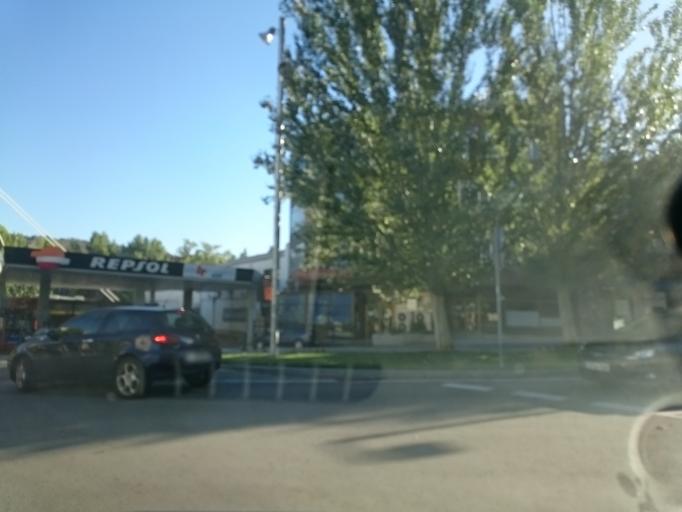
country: ES
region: Catalonia
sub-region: Provincia de Barcelona
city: Martorell
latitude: 41.4774
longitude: 1.9214
